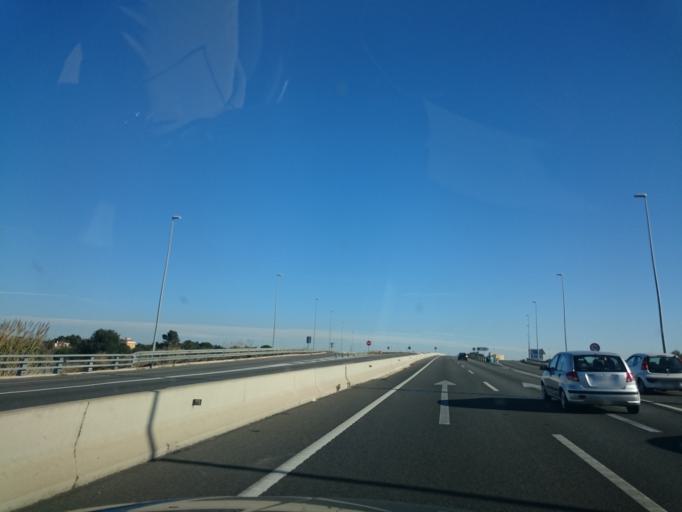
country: ES
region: Catalonia
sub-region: Provincia de Tarragona
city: Vila-seca
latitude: 41.1013
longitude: 1.1238
